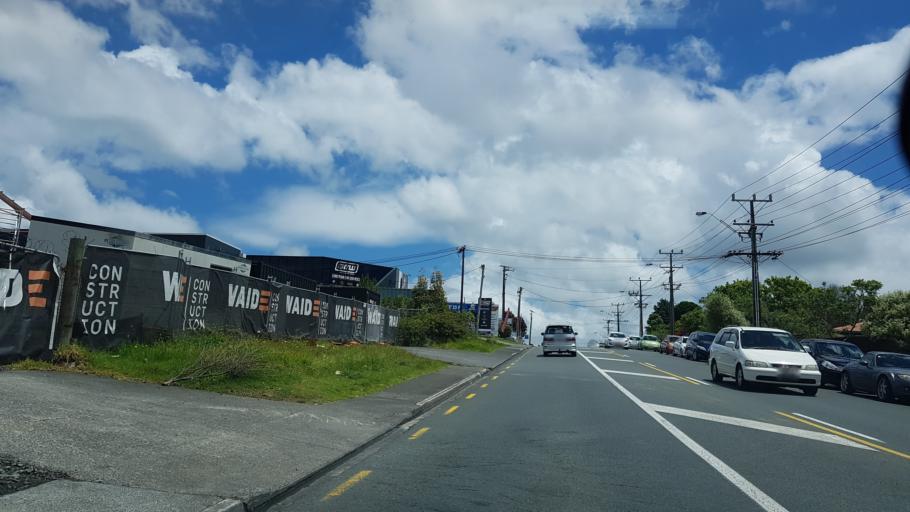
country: NZ
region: Auckland
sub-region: Auckland
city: North Shore
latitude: -36.7812
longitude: 174.7389
